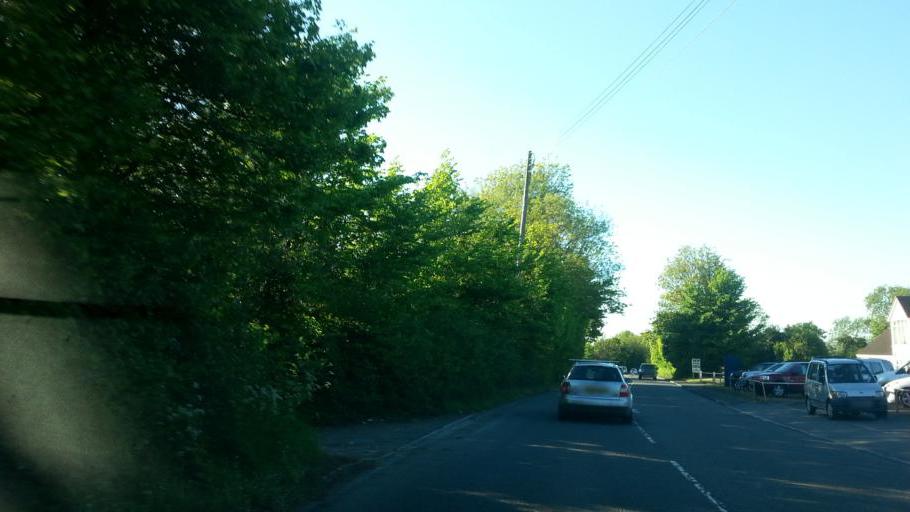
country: GB
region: England
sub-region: Bath and North East Somerset
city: Publow
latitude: 51.3943
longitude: -2.5497
